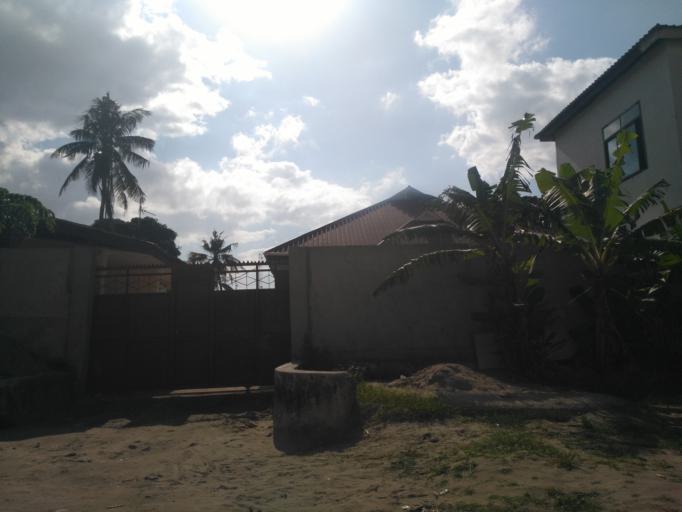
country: TZ
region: Dar es Salaam
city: Magomeni
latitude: -6.7813
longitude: 39.2664
